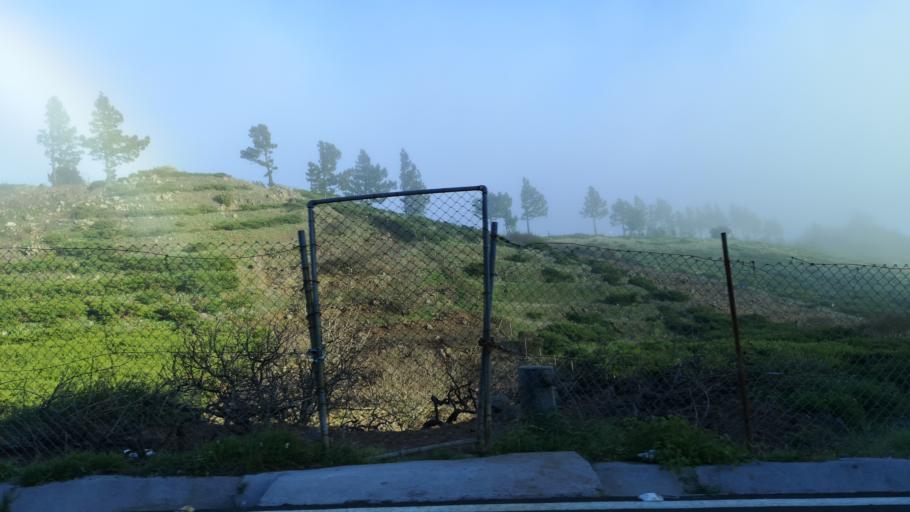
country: ES
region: Canary Islands
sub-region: Provincia de Santa Cruz de Tenerife
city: Alajero
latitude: 28.0990
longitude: -17.2482
